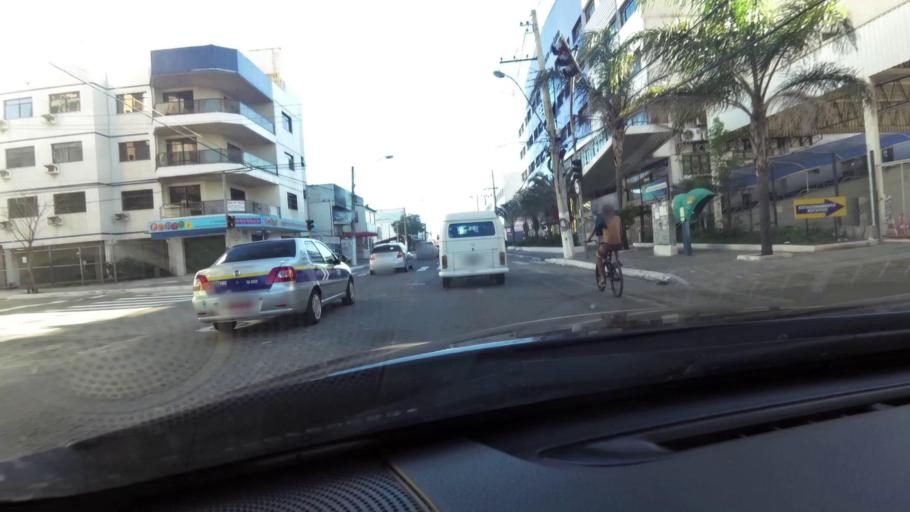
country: BR
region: Espirito Santo
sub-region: Vila Velha
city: Vila Velha
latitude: -20.3590
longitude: -40.2980
